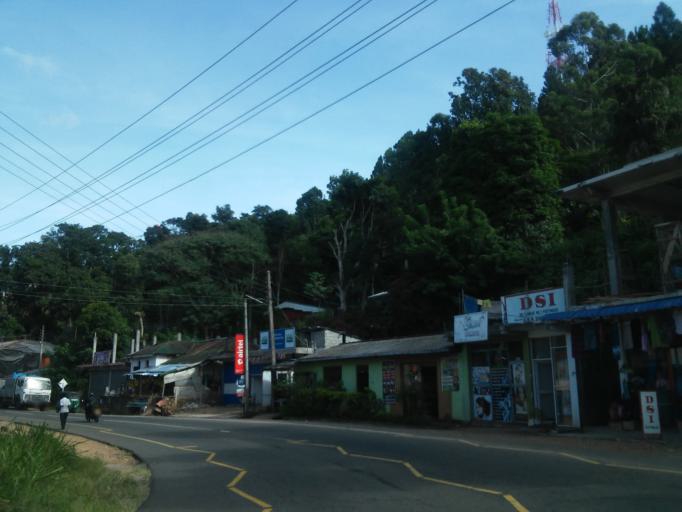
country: LK
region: Uva
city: Haputale
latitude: 6.7608
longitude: 80.8824
